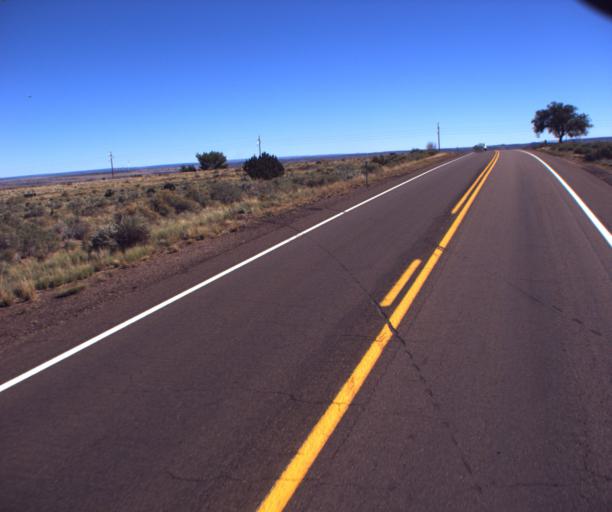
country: US
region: Arizona
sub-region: Apache County
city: Saint Johns
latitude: 34.5060
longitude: -109.4136
